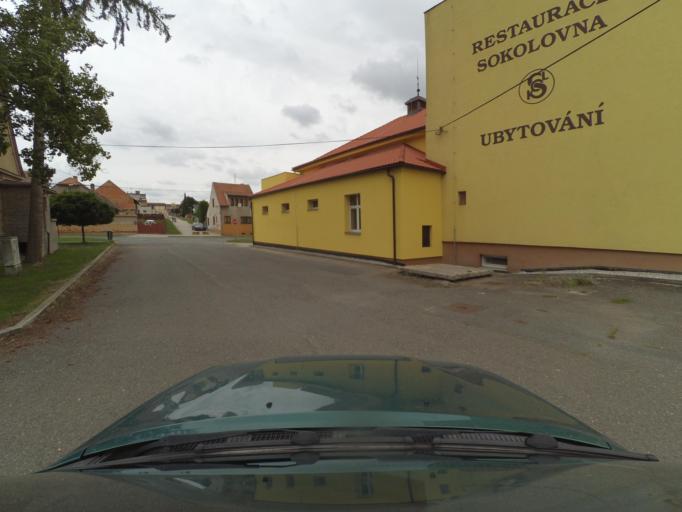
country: CZ
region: Plzensky
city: Kozlany
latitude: 49.9934
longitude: 13.5402
